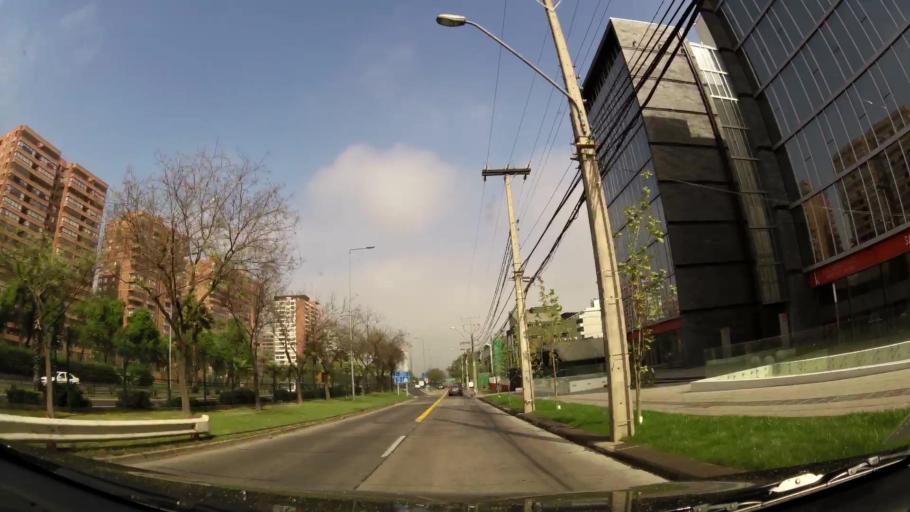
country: CL
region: Santiago Metropolitan
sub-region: Provincia de Santiago
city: Villa Presidente Frei, Nunoa, Santiago, Chile
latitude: -33.3949
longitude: -70.5633
